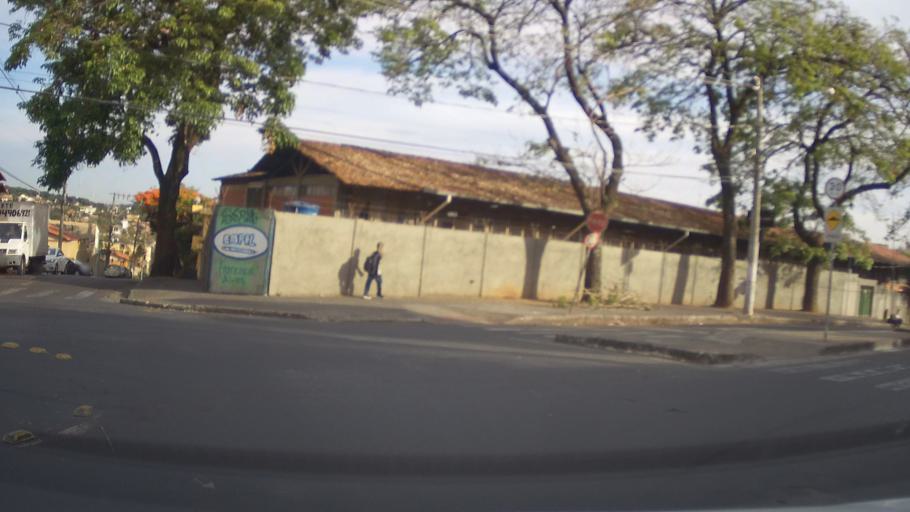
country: BR
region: Minas Gerais
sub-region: Belo Horizonte
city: Belo Horizonte
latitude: -19.8685
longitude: -43.9971
